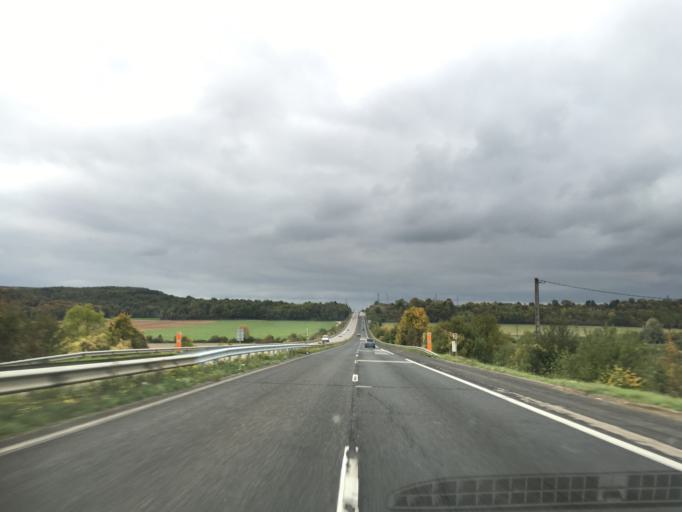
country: FR
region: Lorraine
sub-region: Departement de Meurthe-et-Moselle
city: Foug
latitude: 48.6766
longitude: 5.7609
